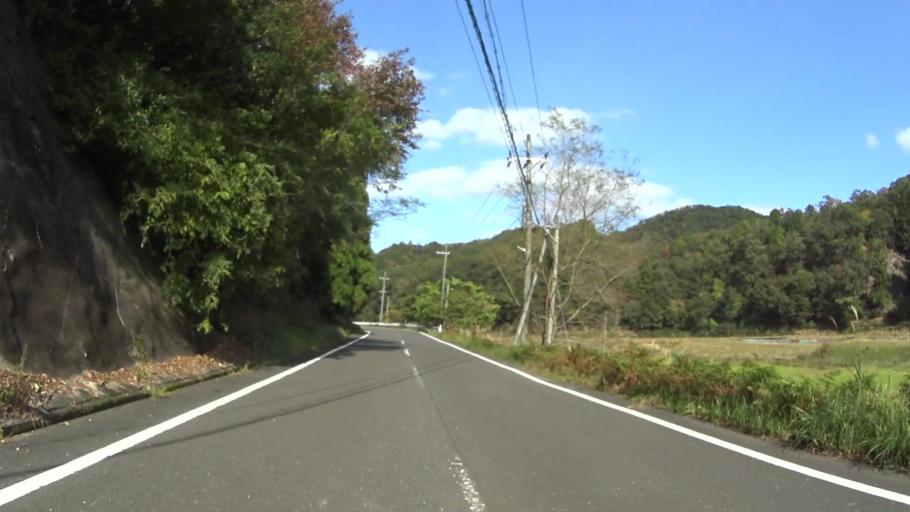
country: JP
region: Hyogo
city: Toyooka
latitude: 35.5577
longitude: 134.9793
